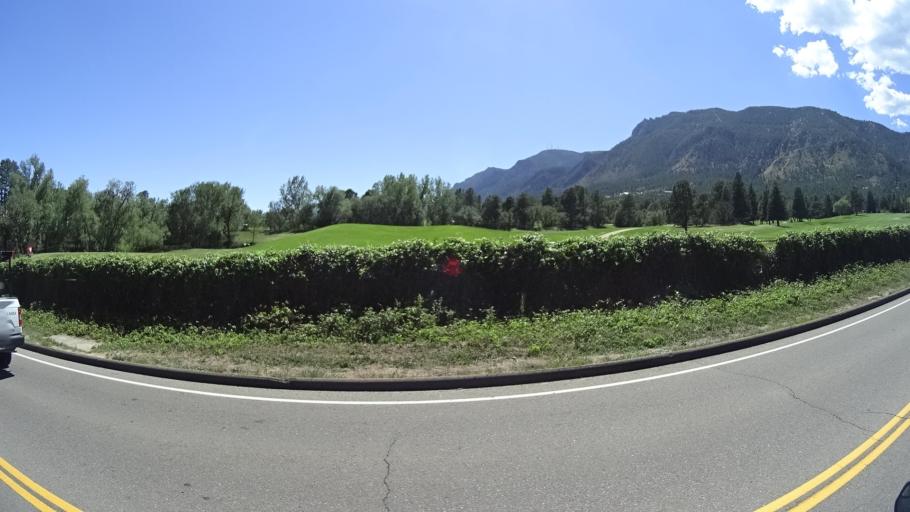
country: US
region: Colorado
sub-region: El Paso County
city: Colorado Springs
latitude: 38.7813
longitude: -104.8490
